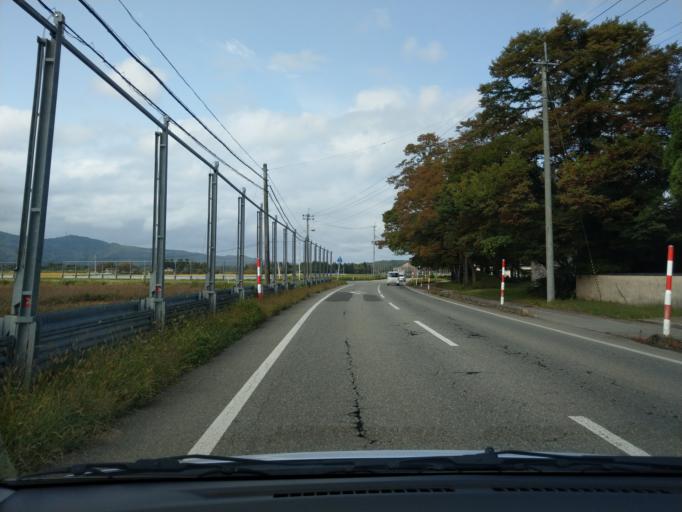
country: JP
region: Akita
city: Omagari
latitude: 39.5291
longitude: 140.2607
